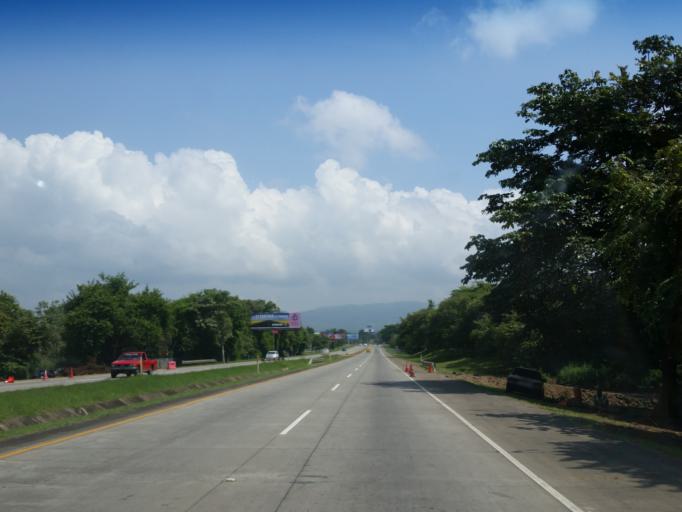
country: PA
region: Panama
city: Tocumen
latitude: 9.0591
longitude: -79.4027
